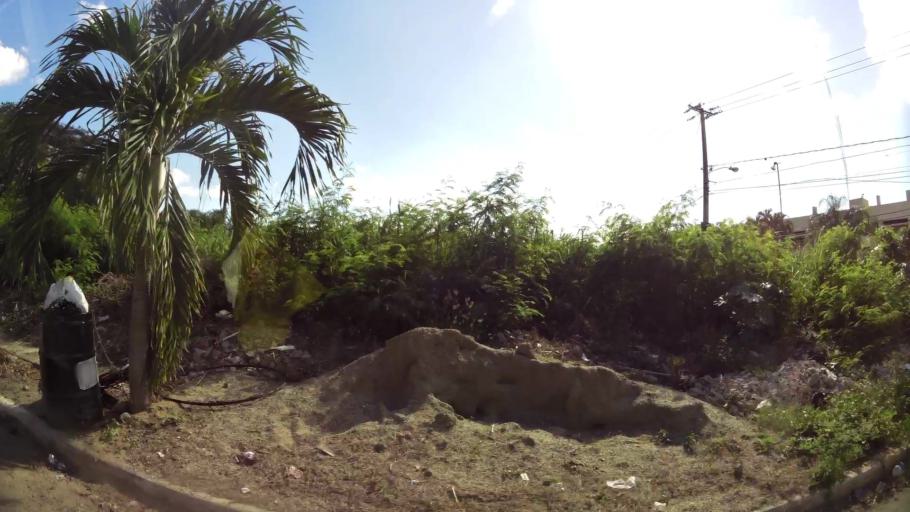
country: DO
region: Santiago
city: Santiago de los Caballeros
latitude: 19.4471
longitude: -70.6730
